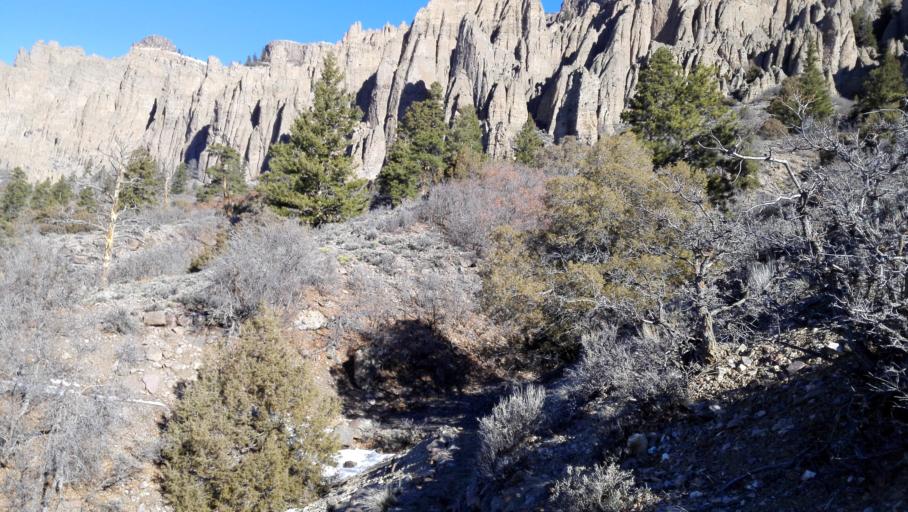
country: US
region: Colorado
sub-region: Gunnison County
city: Gunnison
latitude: 38.4820
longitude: -107.2654
